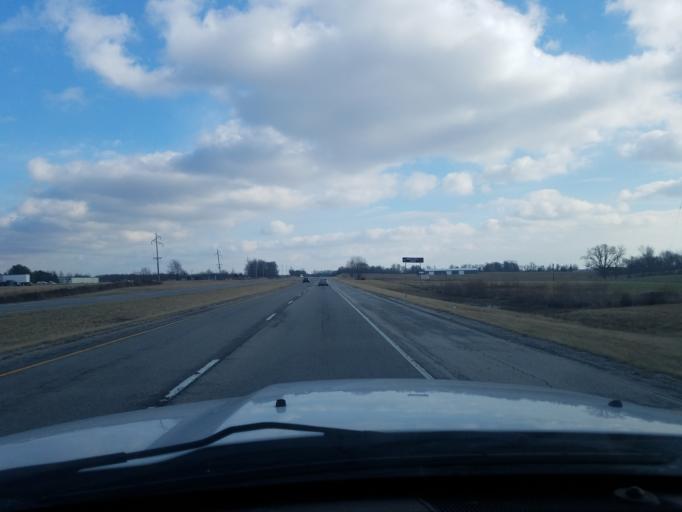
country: US
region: Kentucky
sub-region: Larue County
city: Hodgenville
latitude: 37.5953
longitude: -85.7710
